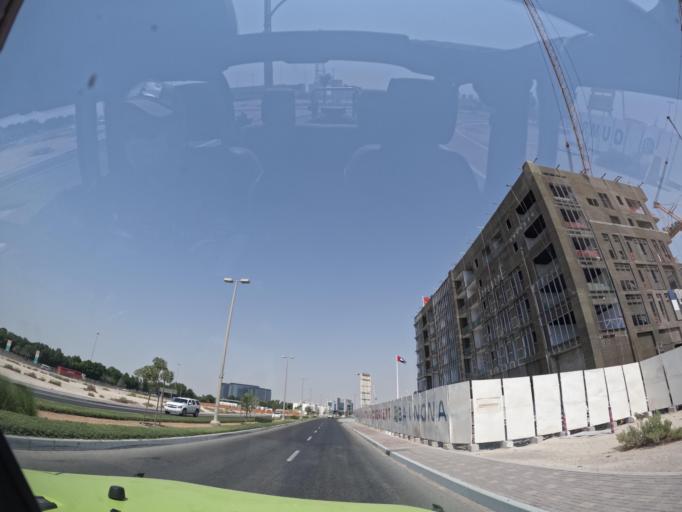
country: AE
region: Abu Dhabi
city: Abu Dhabi
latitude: 24.3154
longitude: 54.6086
